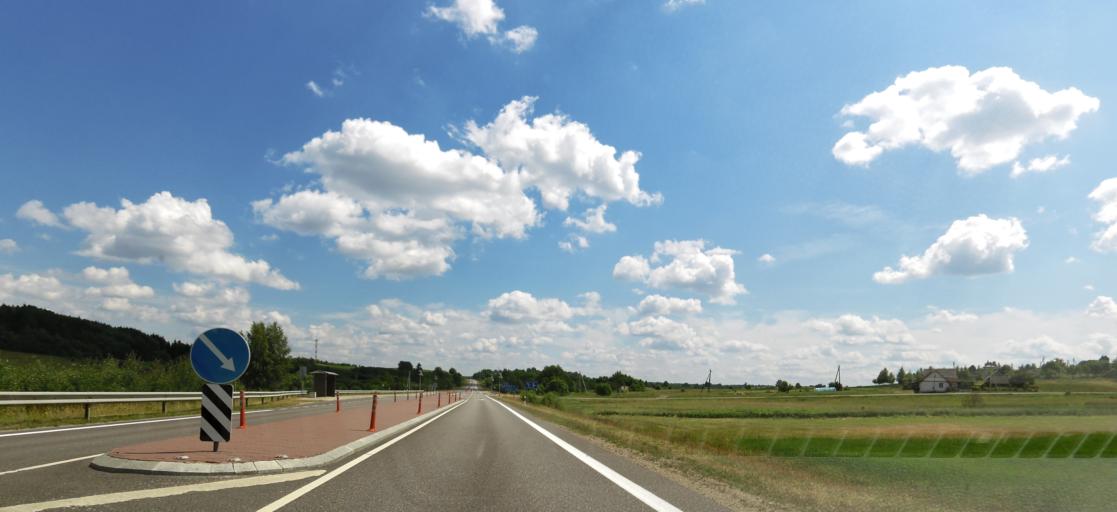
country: LT
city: Skaidiskes
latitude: 54.5812
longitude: 25.5905
